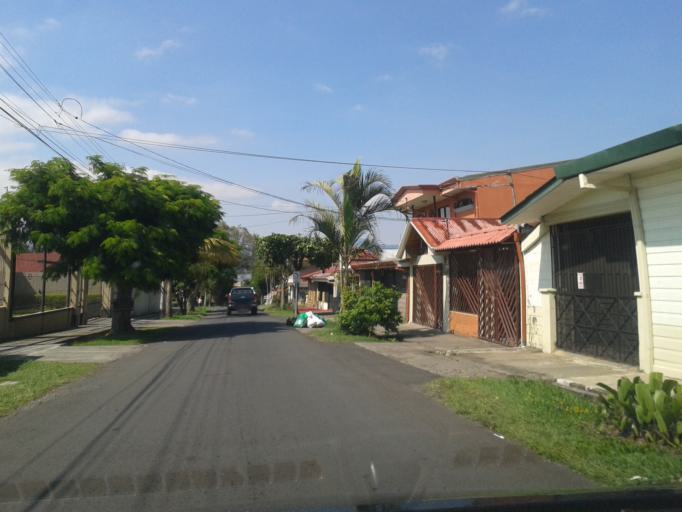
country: CR
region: Heredia
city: Llorente
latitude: 10.0028
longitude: -84.1511
